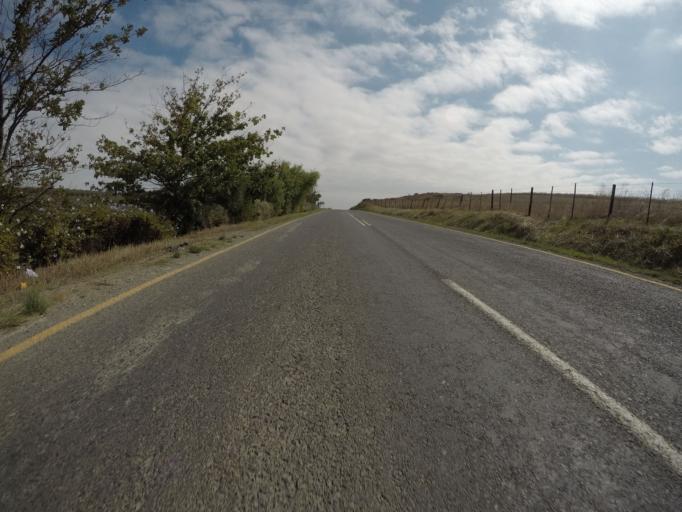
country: ZA
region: Western Cape
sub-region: City of Cape Town
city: Sunset Beach
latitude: -33.7851
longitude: 18.5761
